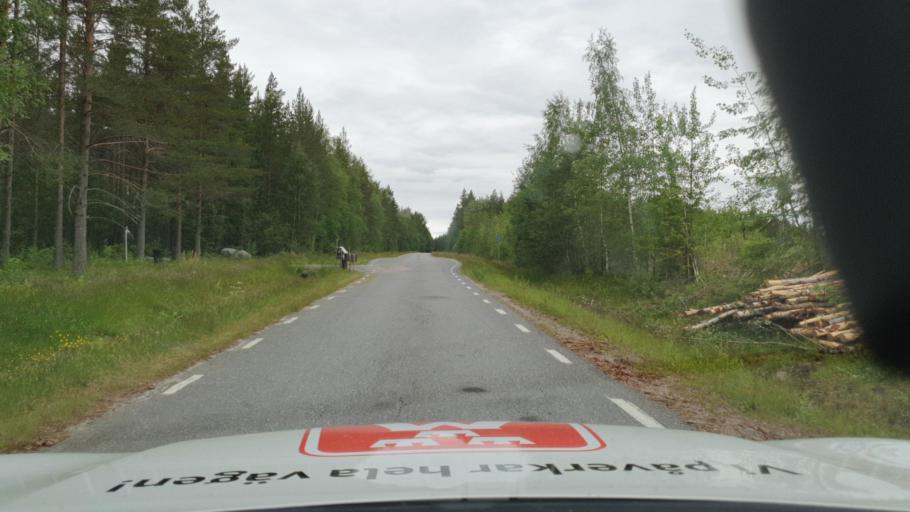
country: SE
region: Vaesterbotten
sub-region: Nordmalings Kommun
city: Nordmaling
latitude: 63.4745
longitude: 19.4607
